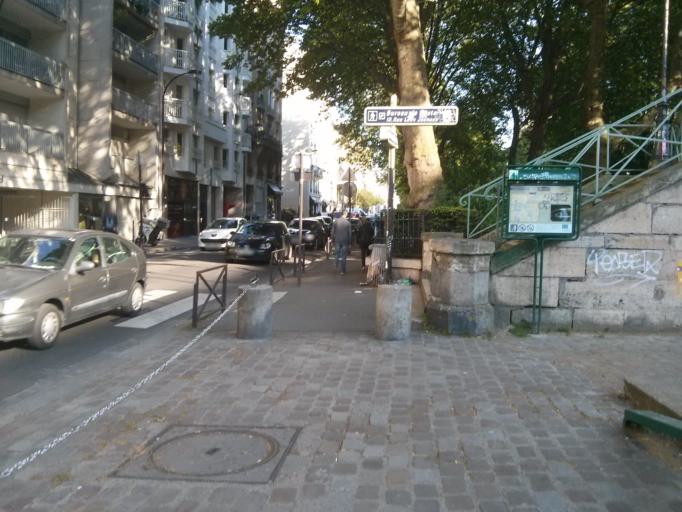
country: FR
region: Ile-de-France
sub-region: Paris
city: Paris
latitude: 48.8699
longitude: 2.3666
